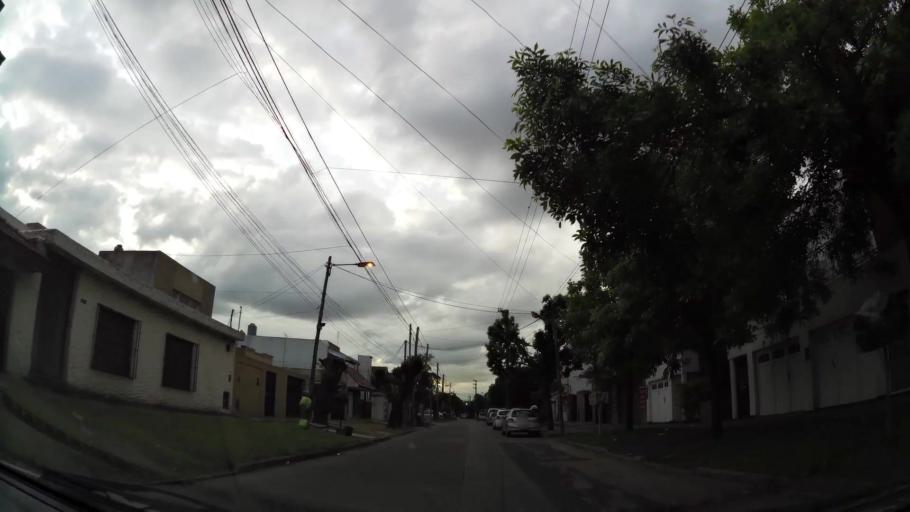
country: AR
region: Buenos Aires
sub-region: Partido de Quilmes
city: Quilmes
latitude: -34.7366
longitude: -58.2462
